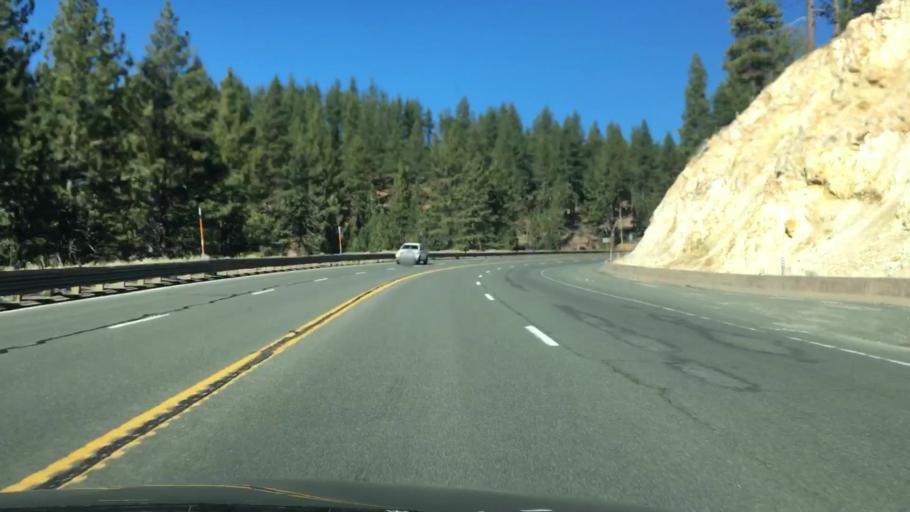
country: US
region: Nevada
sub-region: Douglas County
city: Kingsbury
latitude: 39.0942
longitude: -119.9104
